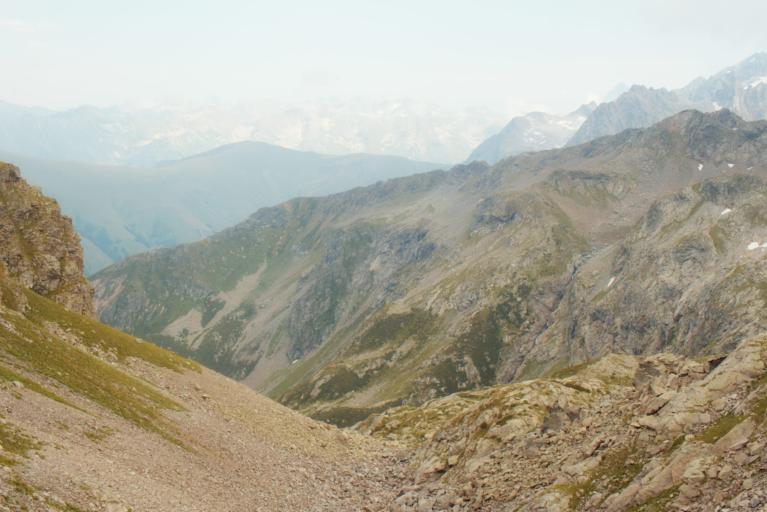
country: RU
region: Karachayevo-Cherkesiya
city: Nizhniy Arkhyz
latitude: 43.4576
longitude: 41.2272
